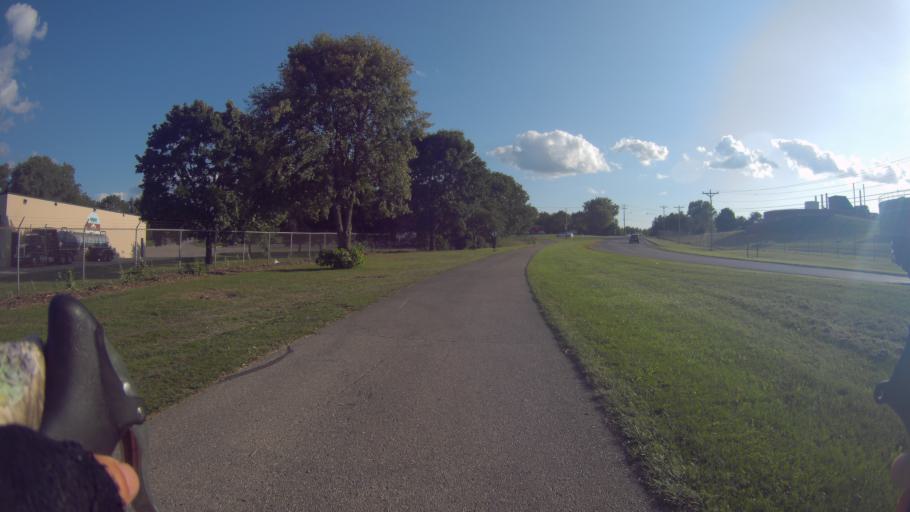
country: US
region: Wisconsin
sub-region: Dane County
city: Monona
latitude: 43.0335
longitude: -89.3539
